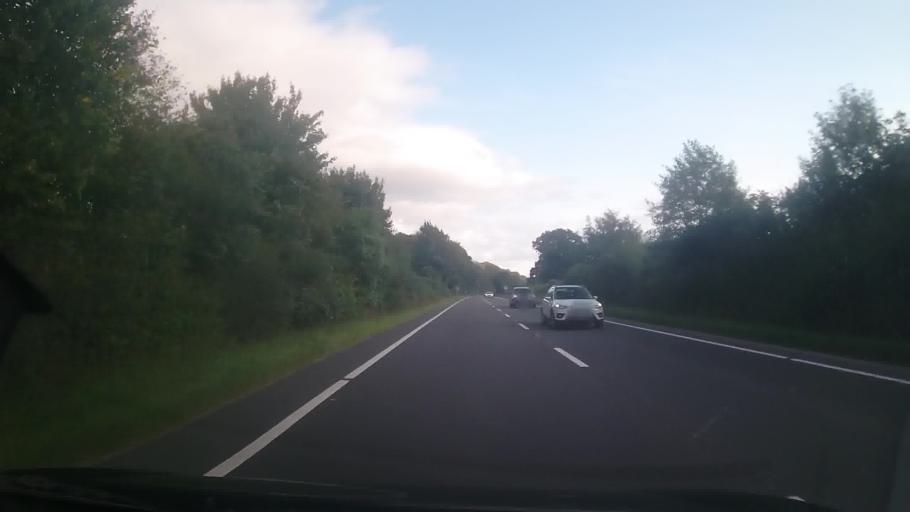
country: GB
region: England
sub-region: Shropshire
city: Craven Arms
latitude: 52.4154
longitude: -2.8138
